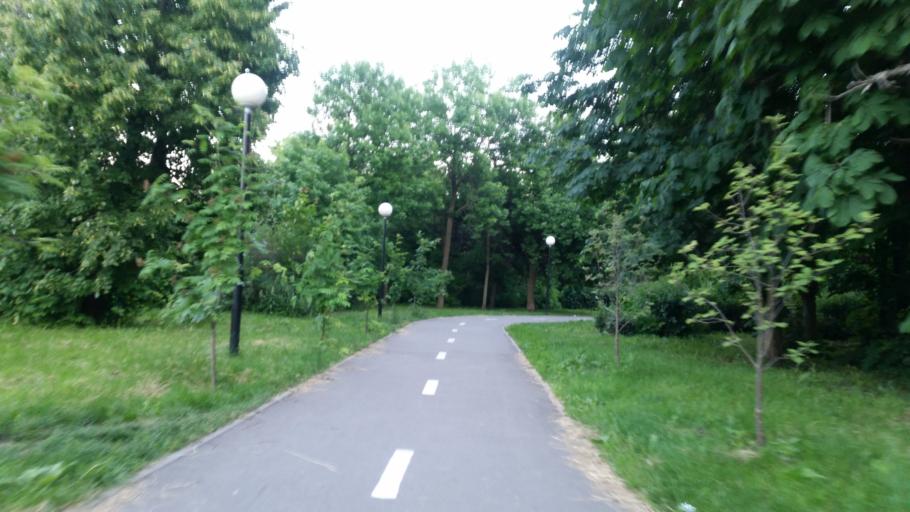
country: RU
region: Ulyanovsk
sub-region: Ulyanovskiy Rayon
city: Ulyanovsk
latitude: 54.3292
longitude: 48.4074
